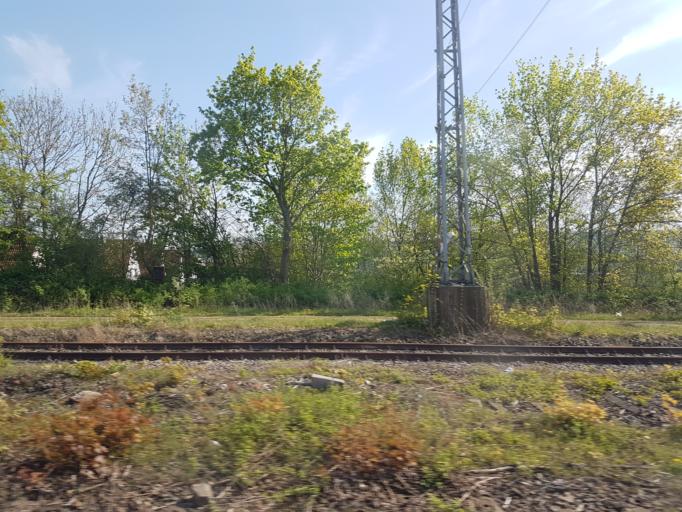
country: DE
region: Lower Saxony
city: Springe
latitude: 52.2157
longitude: 9.5626
